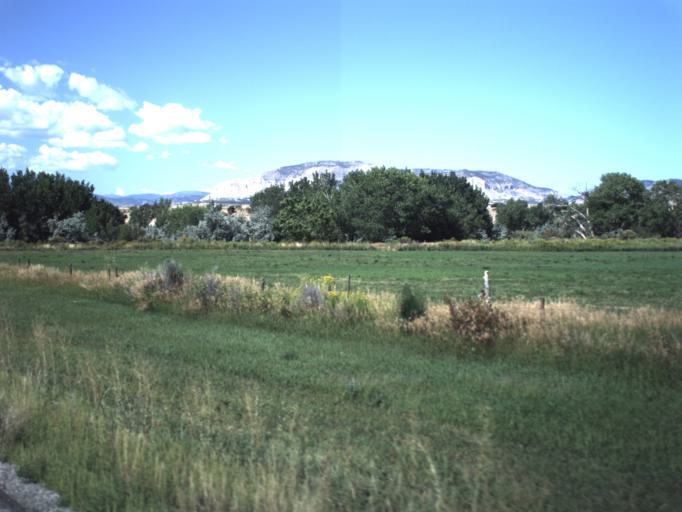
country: US
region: Utah
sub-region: Emery County
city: Ferron
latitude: 38.9018
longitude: -111.2738
